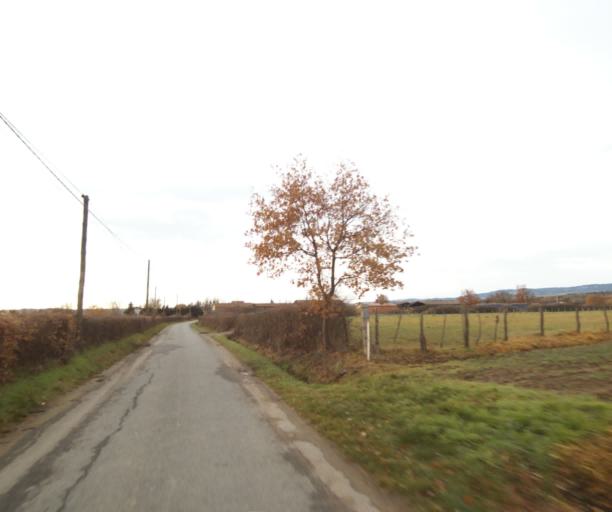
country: FR
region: Rhone-Alpes
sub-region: Departement de la Loire
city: Sury-le-Comtal
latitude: 45.5311
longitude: 4.1664
